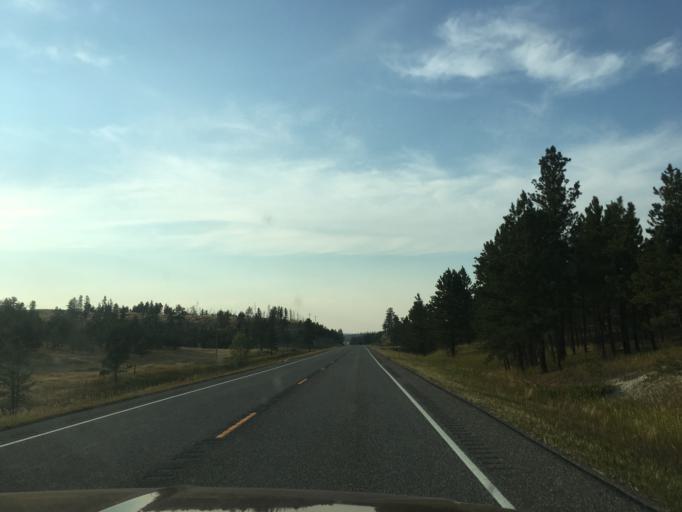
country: US
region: Montana
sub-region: Musselshell County
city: Roundup
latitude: 46.2736
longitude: -108.4727
